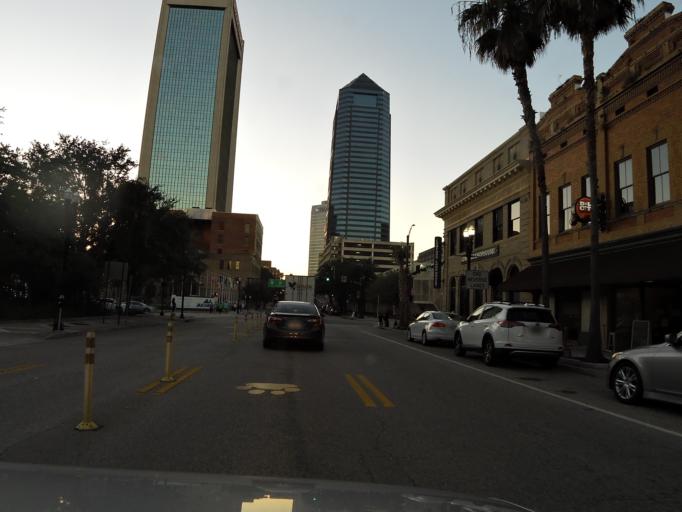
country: US
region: Florida
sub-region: Duval County
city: Jacksonville
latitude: 30.3258
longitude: -81.6563
